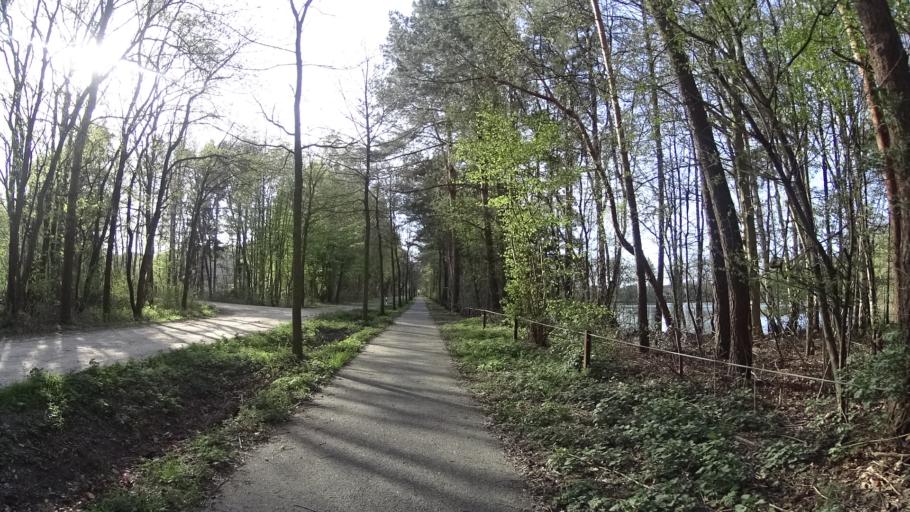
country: DE
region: Lower Saxony
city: Haren
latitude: 52.7937
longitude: 7.2697
